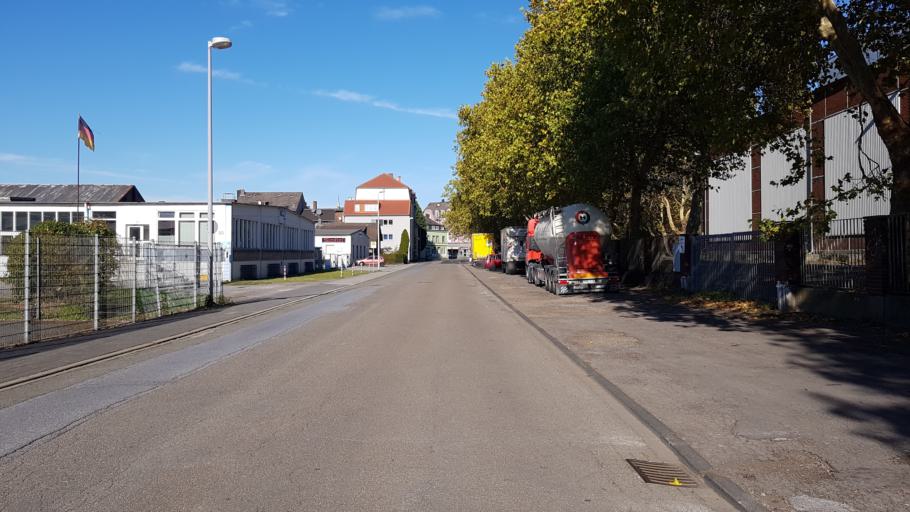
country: DE
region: North Rhine-Westphalia
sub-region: Regierungsbezirk Dusseldorf
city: Muelheim (Ruhr)
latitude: 51.4471
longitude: 6.8670
